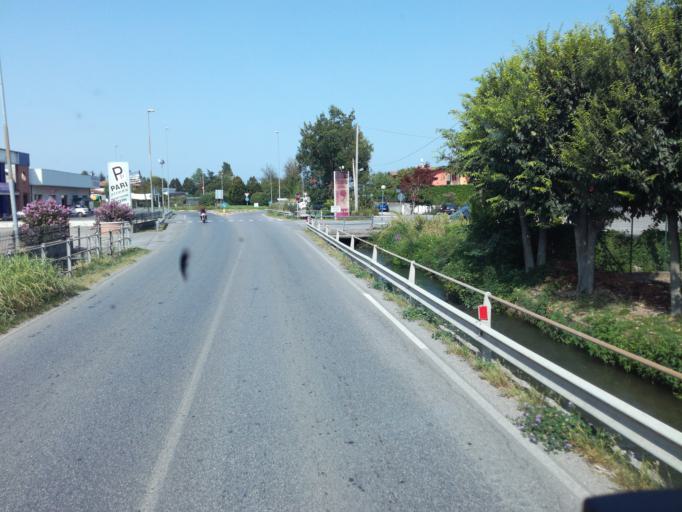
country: IT
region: Lombardy
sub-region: Provincia di Brescia
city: Dello
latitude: 45.4201
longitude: 10.0820
